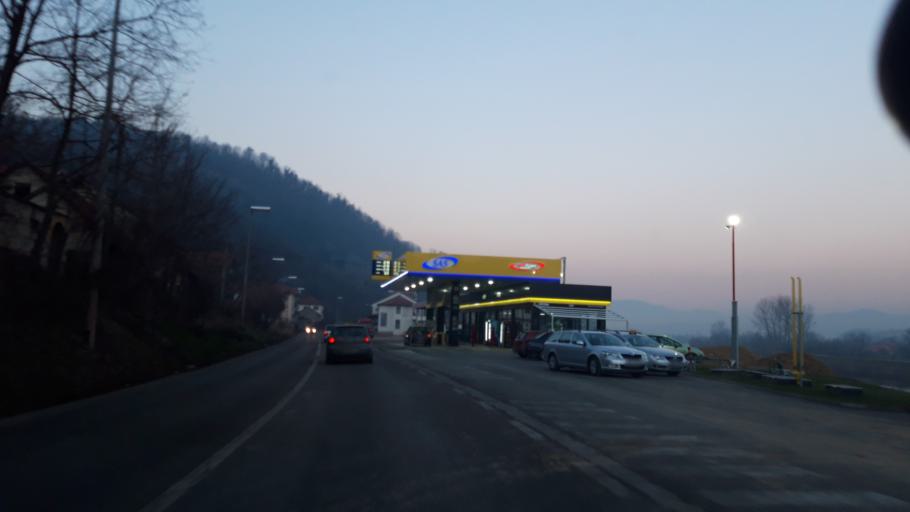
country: BA
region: Republika Srpska
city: Zvornik
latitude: 44.3954
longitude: 19.1072
